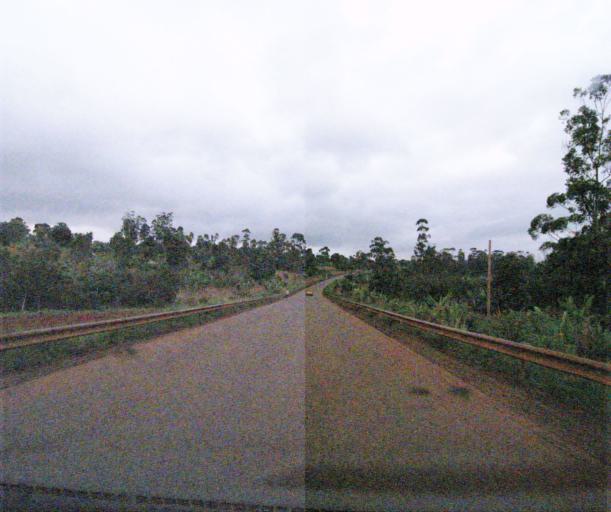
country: CM
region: West
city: Bansoa
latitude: 5.4987
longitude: 10.2327
